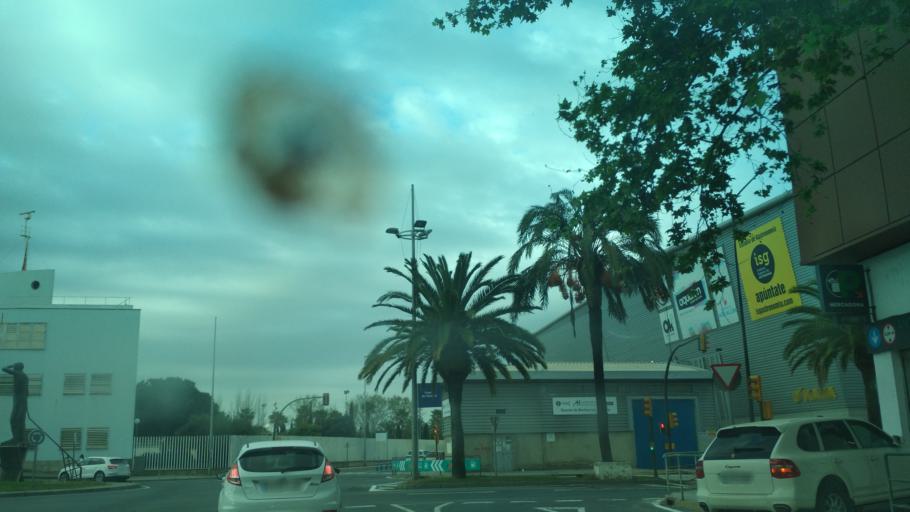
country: ES
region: Andalusia
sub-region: Provincia de Huelva
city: Huelva
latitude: 37.2625
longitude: -6.9594
